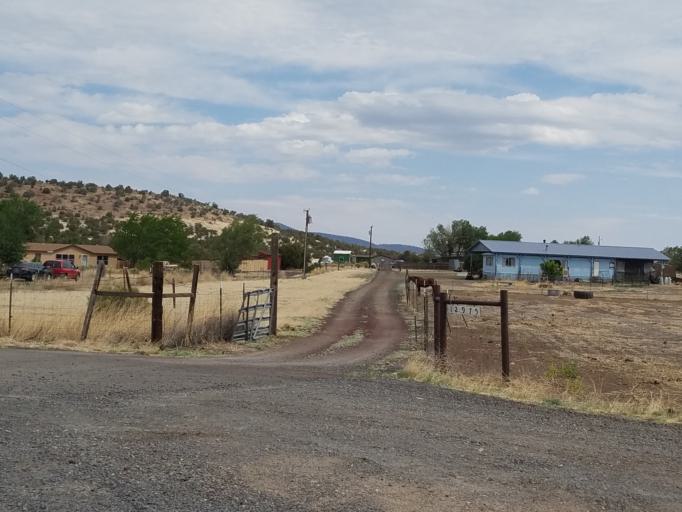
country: US
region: Arizona
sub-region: Coconino County
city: Flagstaff
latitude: 35.2121
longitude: -111.4184
